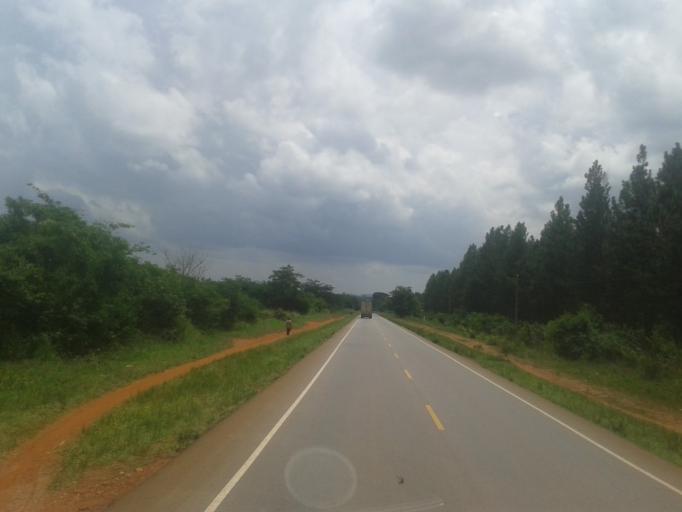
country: UG
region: Central Region
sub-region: Nakasongola District
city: Nakasongola
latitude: 1.1895
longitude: 32.4612
